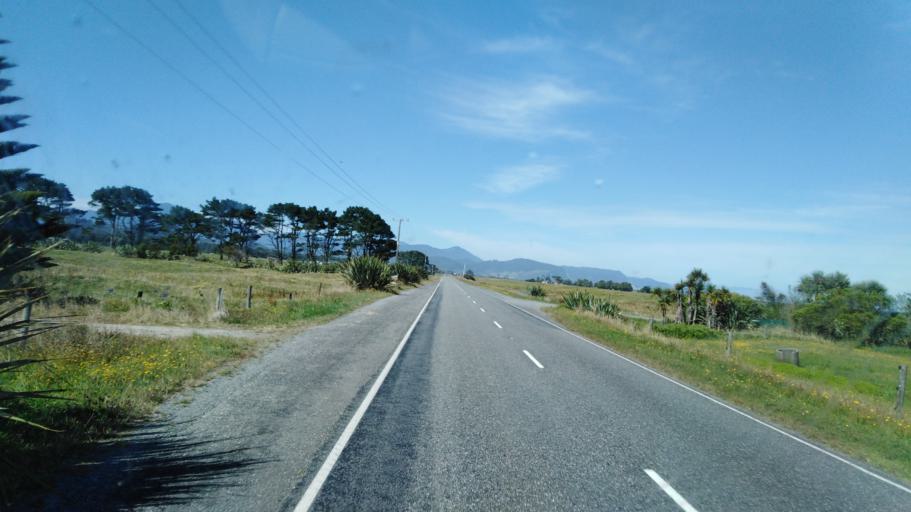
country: NZ
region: West Coast
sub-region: Buller District
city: Westport
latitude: -41.3031
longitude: 172.0926
